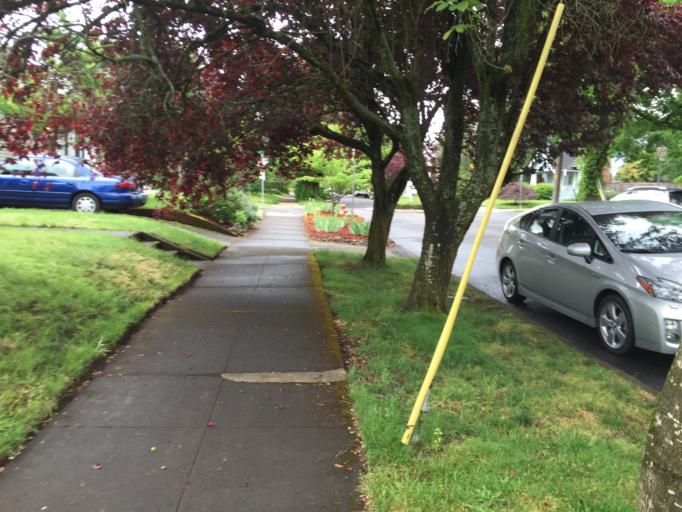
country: US
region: Oregon
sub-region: Multnomah County
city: Lents
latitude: 45.5334
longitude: -122.6087
